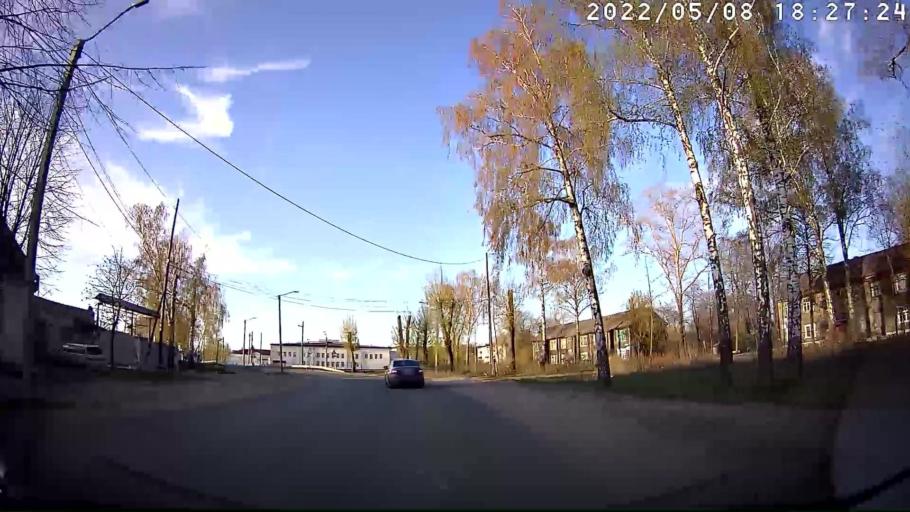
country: RU
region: Mariy-El
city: Volzhsk
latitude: 55.8594
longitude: 48.3714
